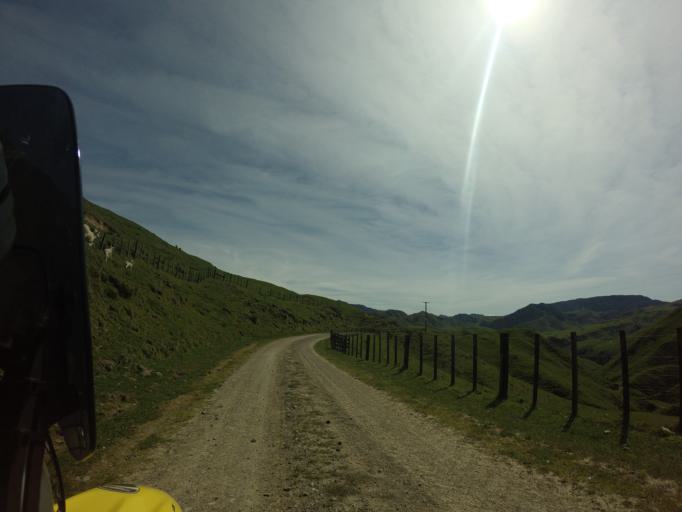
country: NZ
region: Bay of Plenty
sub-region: Opotiki District
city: Opotiki
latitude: -38.4538
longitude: 177.3584
